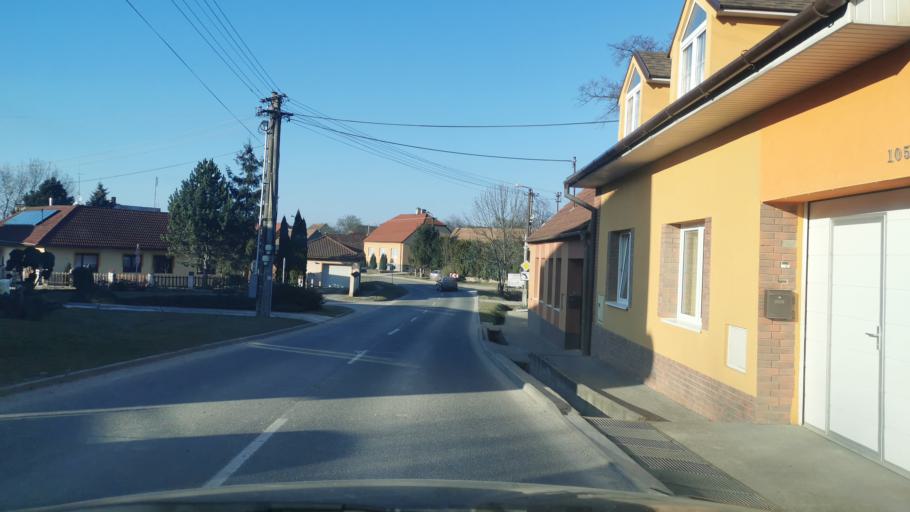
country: SK
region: Trnavsky
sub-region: Okres Skalica
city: Skalica
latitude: 48.8088
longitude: 17.2490
